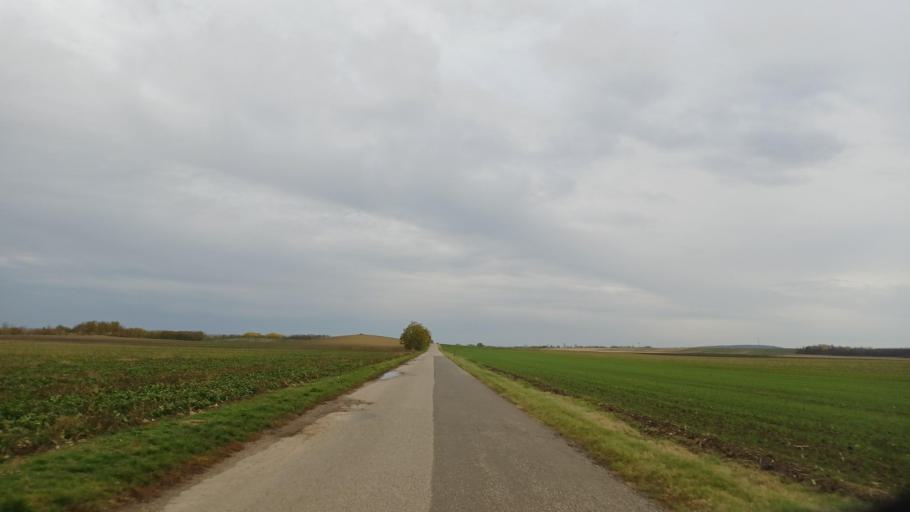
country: HU
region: Tolna
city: Nagydorog
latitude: 46.6620
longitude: 18.6051
